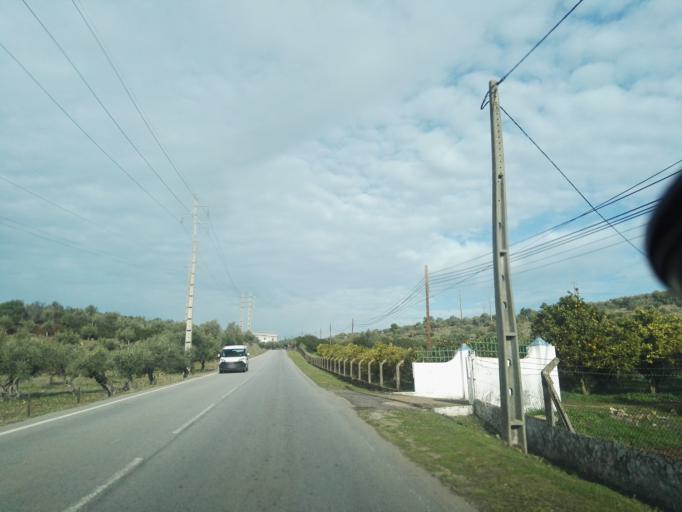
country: PT
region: Portalegre
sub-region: Elvas
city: Elvas
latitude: 38.8890
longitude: -7.1697
